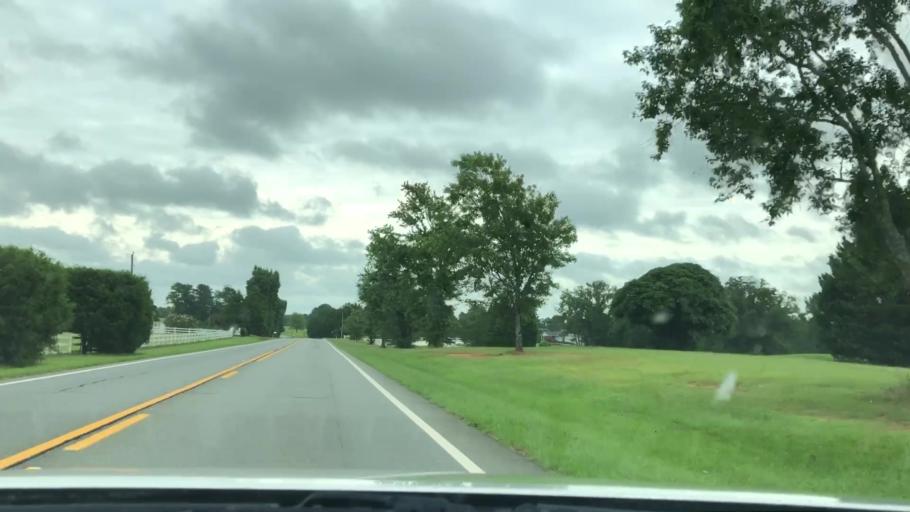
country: US
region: Georgia
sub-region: Pike County
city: Zebulon
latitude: 33.1104
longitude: -84.3914
